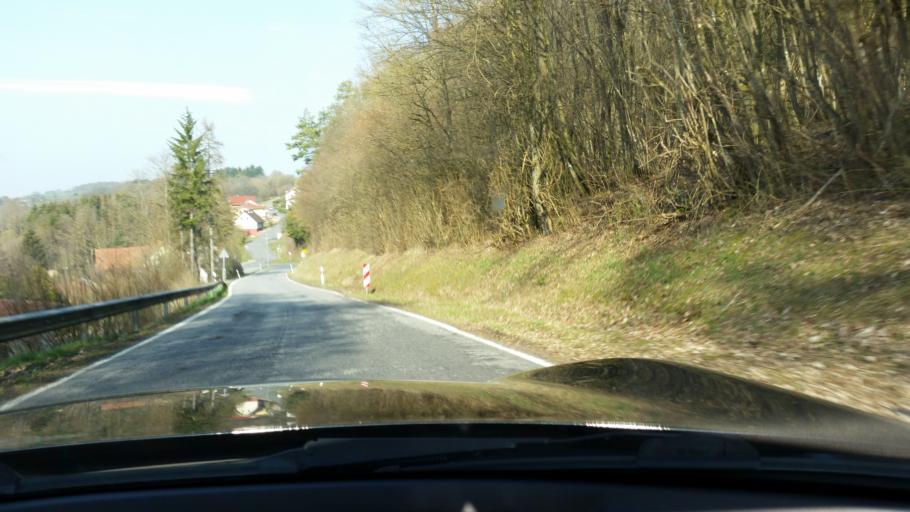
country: DE
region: Baden-Wuerttemberg
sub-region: Karlsruhe Region
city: Billigheim
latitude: 49.3714
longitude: 9.2672
